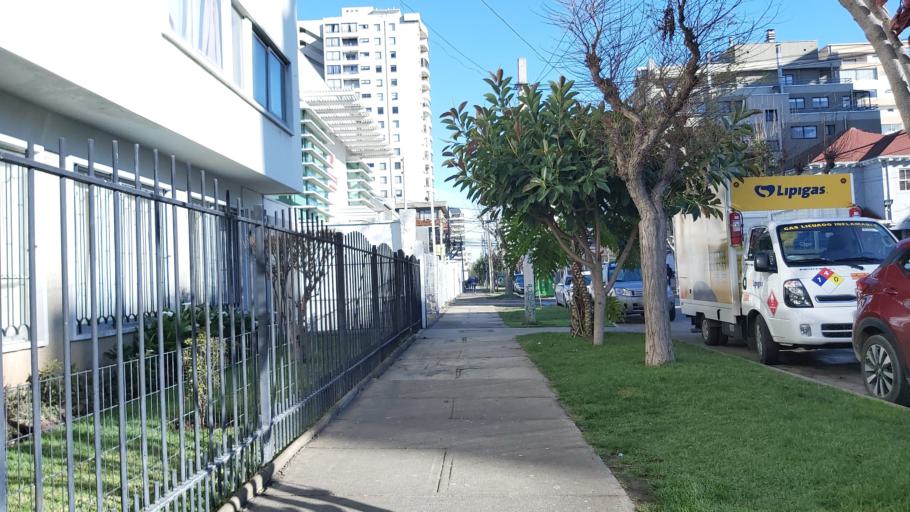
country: CL
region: Valparaiso
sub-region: Provincia de Valparaiso
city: Vina del Mar
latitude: -33.0174
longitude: -71.5509
